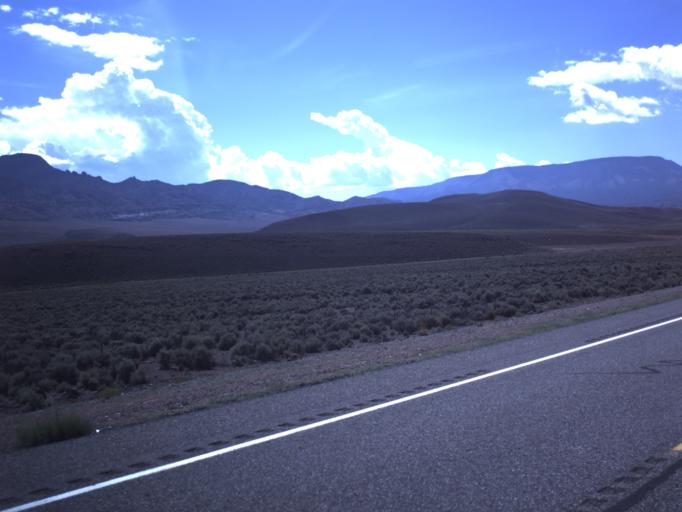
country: US
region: Utah
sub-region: Piute County
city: Junction
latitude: 38.2852
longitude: -112.2250
